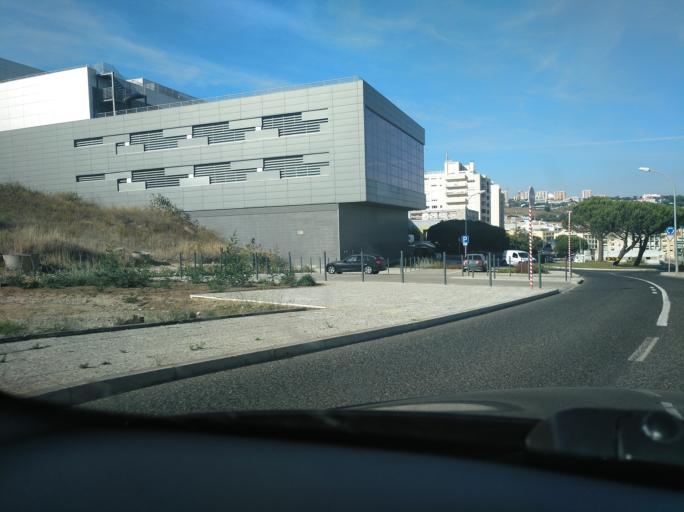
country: PT
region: Lisbon
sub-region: Oeiras
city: Linda-a-Velha
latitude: 38.7177
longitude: -9.2283
